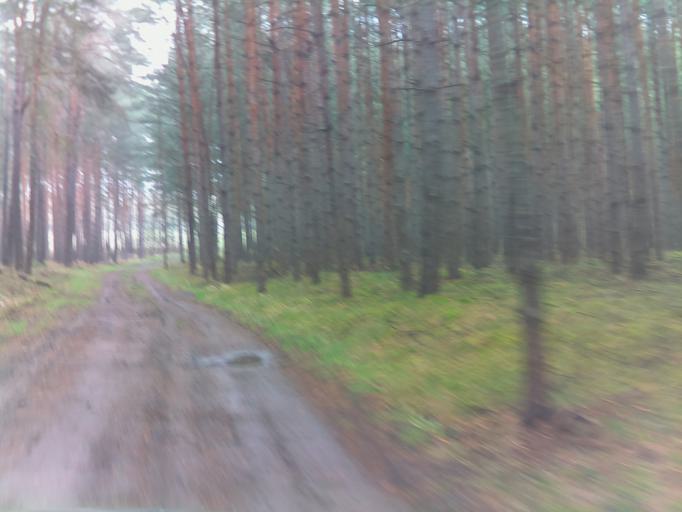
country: DE
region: Brandenburg
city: Schlepzig
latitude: 52.0167
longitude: 13.9862
